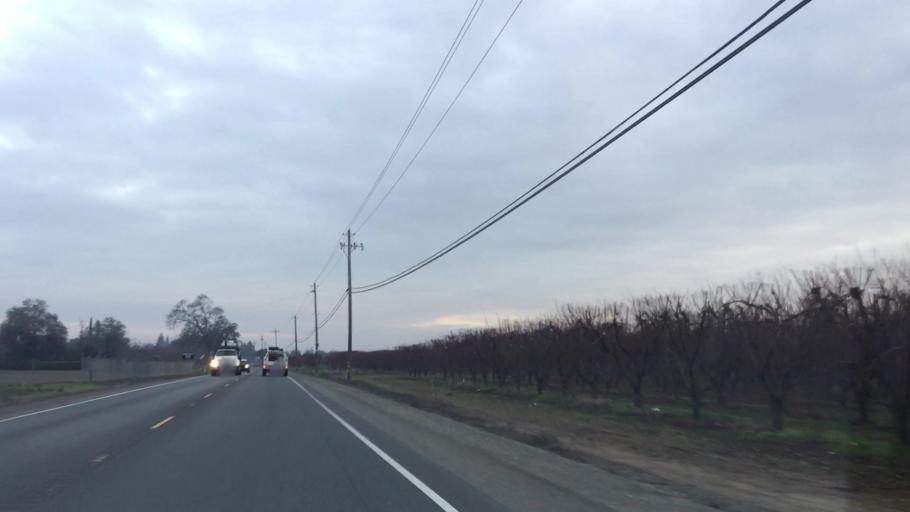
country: US
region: California
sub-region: Sutter County
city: Live Oak
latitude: 39.2872
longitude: -121.5945
